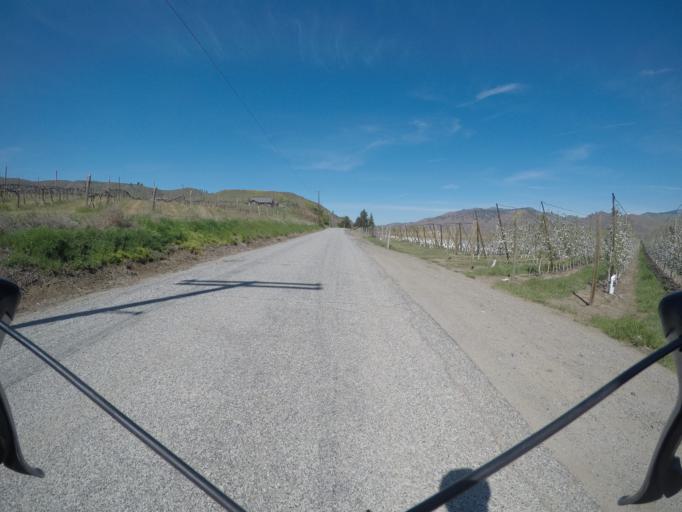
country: US
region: Washington
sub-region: Chelan County
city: Cashmere
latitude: 47.4987
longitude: -120.4345
